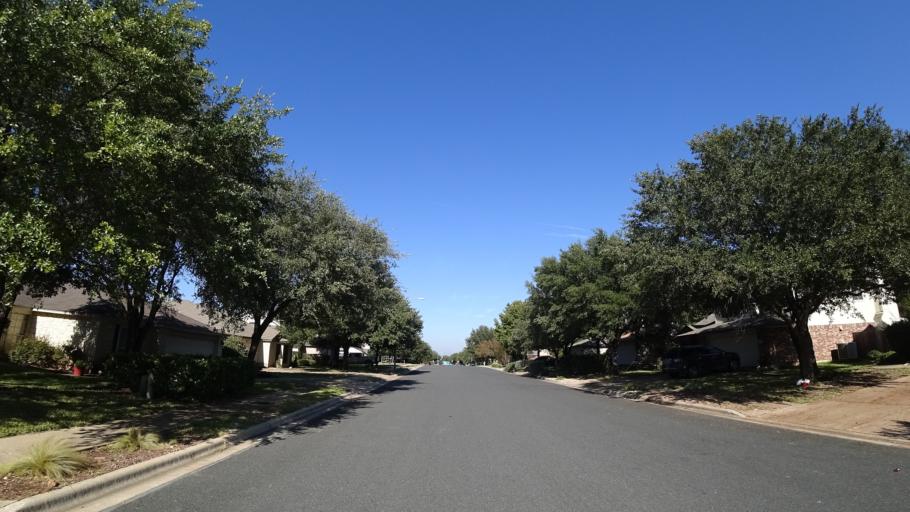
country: US
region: Texas
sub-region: Travis County
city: Shady Hollow
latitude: 30.1978
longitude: -97.8553
